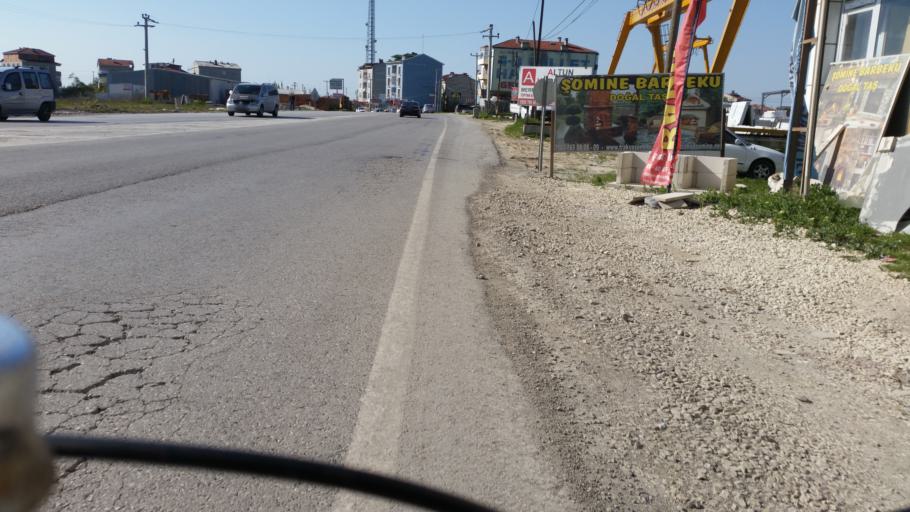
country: TR
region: Tekirdag
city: Cerkezkoey
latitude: 41.3549
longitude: 27.9550
